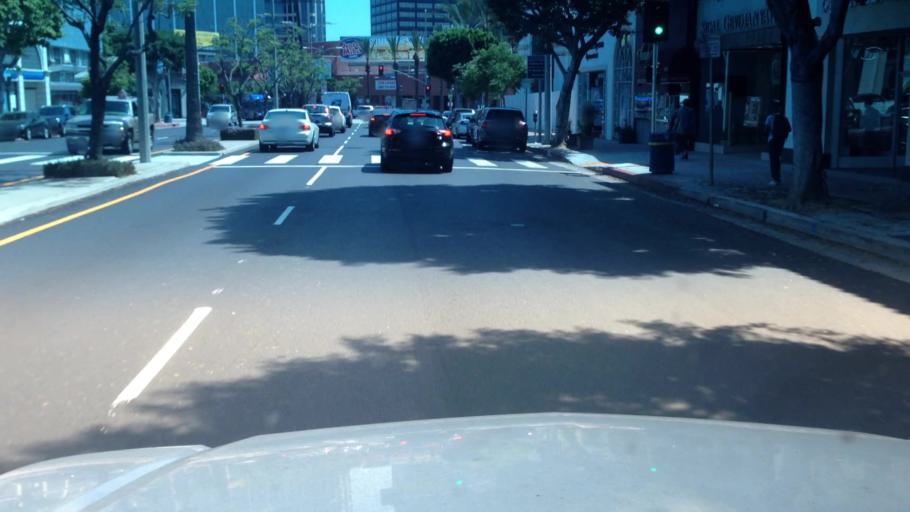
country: US
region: California
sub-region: Los Angeles County
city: Westwood, Los Angeles
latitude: 34.0618
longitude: -118.4455
